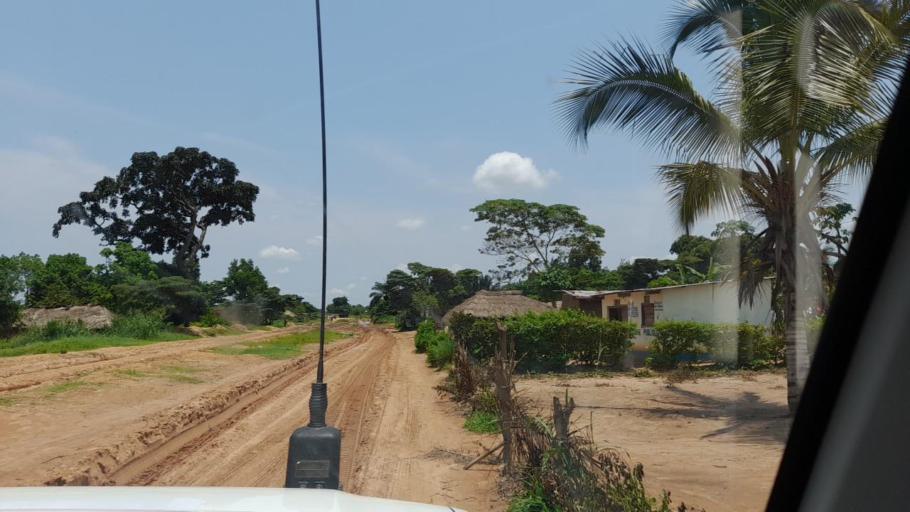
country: CD
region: Kasai-Occidental
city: Kananga
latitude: -5.9480
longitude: 22.2782
